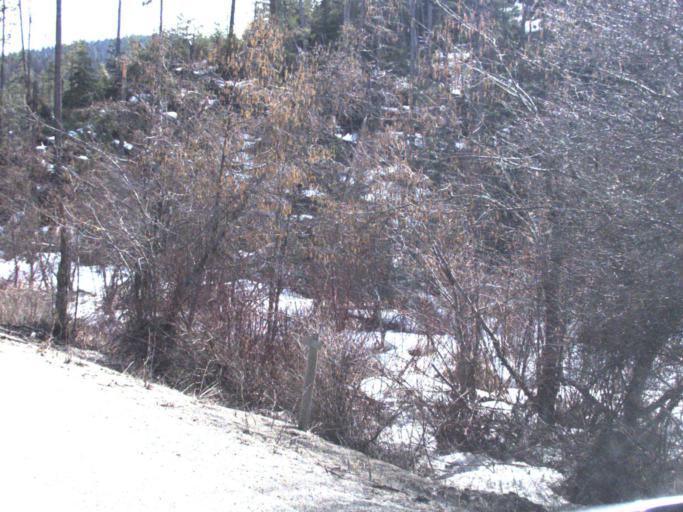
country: US
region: Washington
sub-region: Stevens County
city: Chewelah
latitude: 48.5307
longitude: -117.6220
